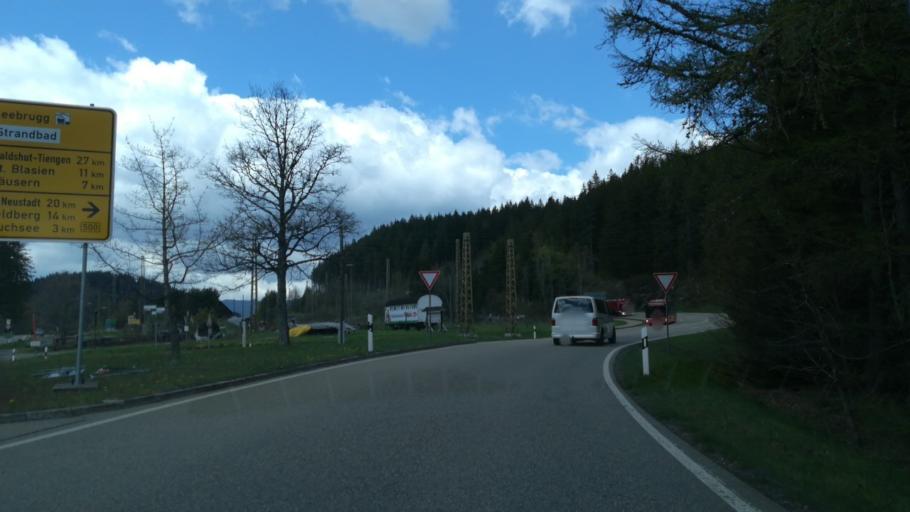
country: DE
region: Baden-Wuerttemberg
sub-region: Freiburg Region
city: Schluchsee
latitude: 47.8004
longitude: 8.1994
